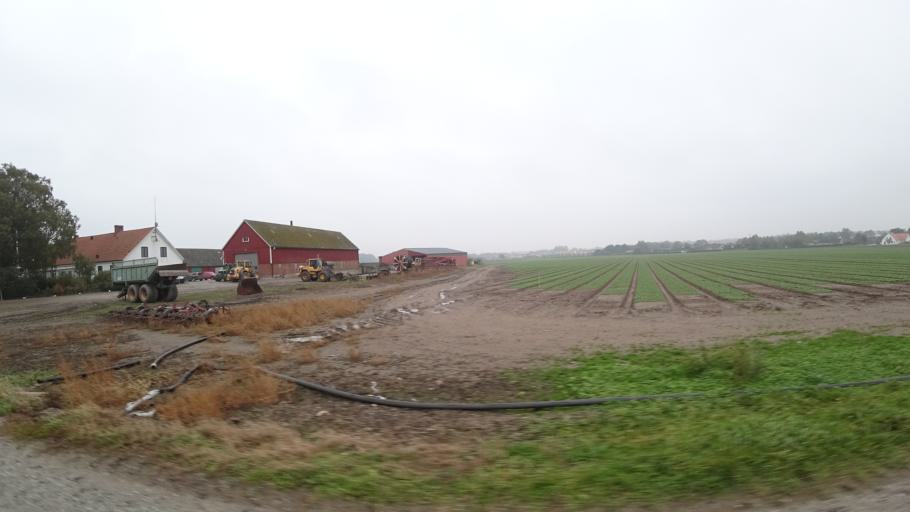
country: SE
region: Skane
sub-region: Kavlinge Kommun
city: Kaevlinge
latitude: 55.8099
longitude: 13.1191
